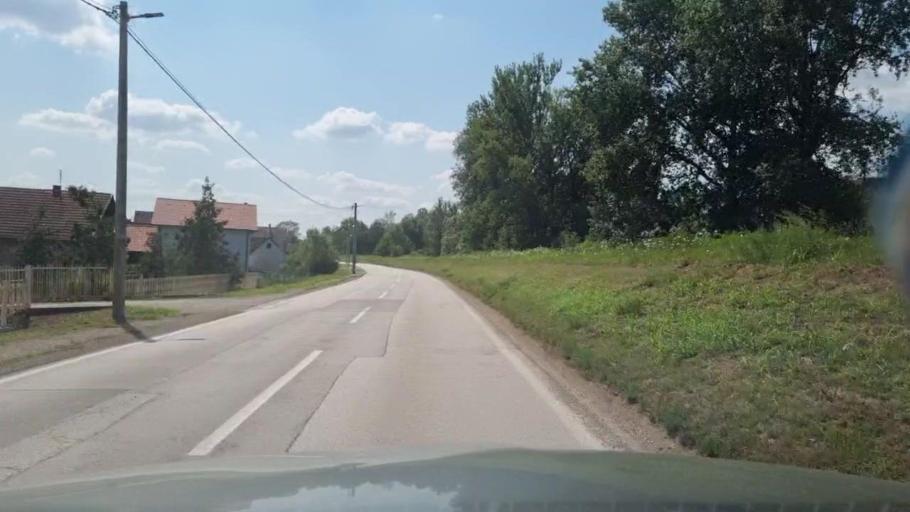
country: BA
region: Republika Srpska
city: Ostra Luka
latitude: 45.0659
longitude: 18.5683
